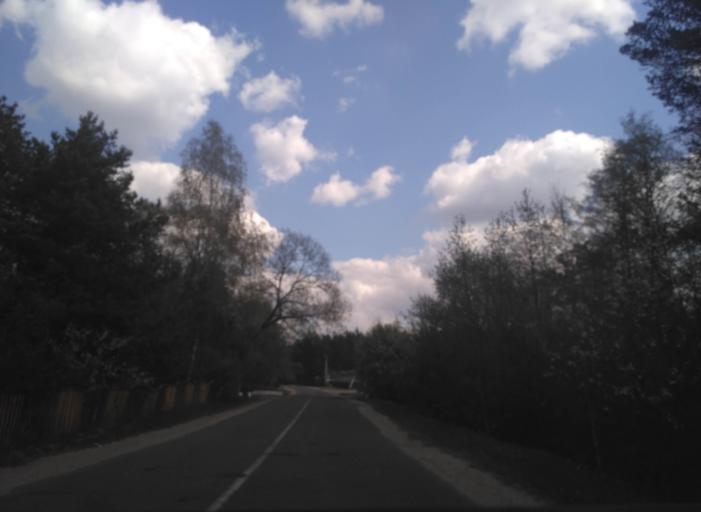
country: BY
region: Minsk
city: Radashkovichy
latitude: 54.1833
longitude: 27.2542
